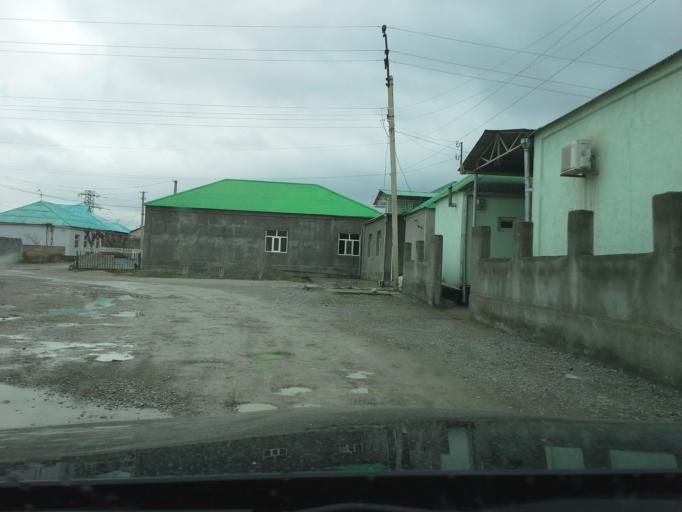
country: TM
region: Ahal
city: Abadan
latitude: 37.9527
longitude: 58.2045
